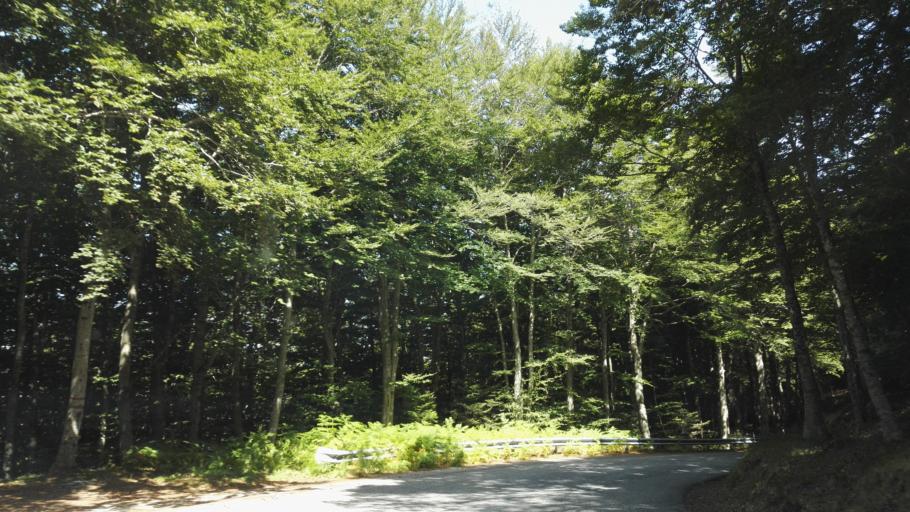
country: IT
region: Calabria
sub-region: Provincia di Vibo-Valentia
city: Mongiana
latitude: 38.5164
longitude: 16.3427
